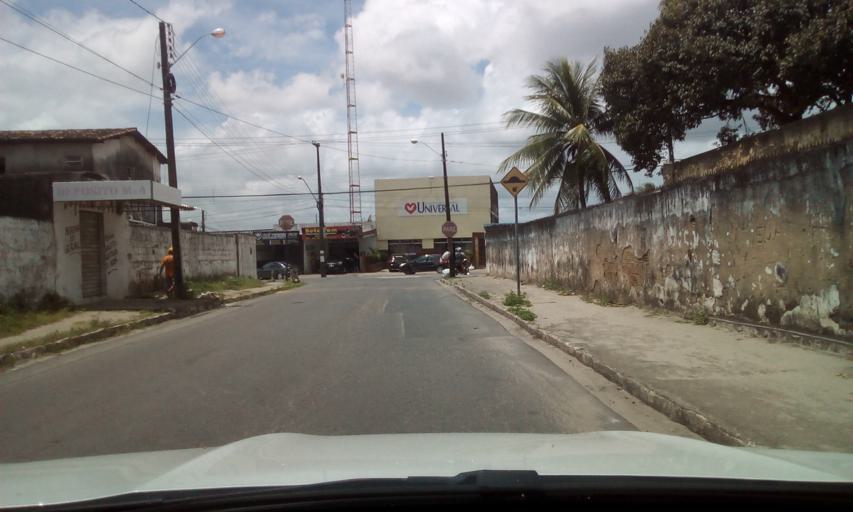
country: BR
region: Paraiba
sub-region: Joao Pessoa
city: Joao Pessoa
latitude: -7.1806
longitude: -34.8814
